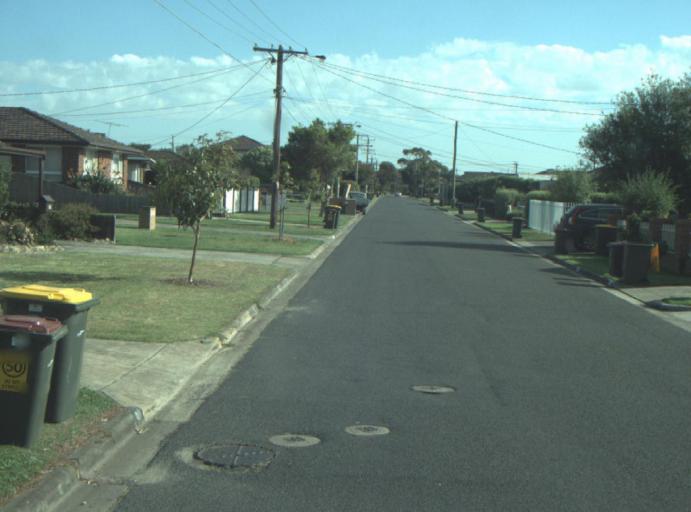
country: AU
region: Victoria
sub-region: Greater Geelong
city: Hamlyn Heights
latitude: -38.1205
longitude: 144.3215
